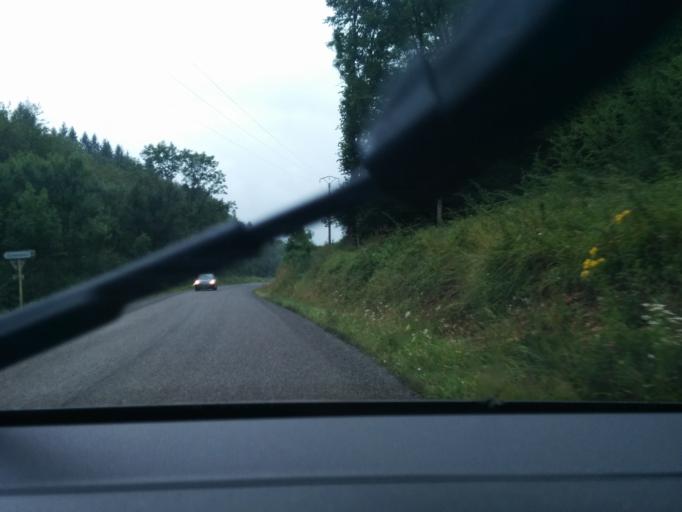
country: FR
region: Franche-Comte
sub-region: Departement du Jura
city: Valfin-les-Saint-Claude
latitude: 46.4446
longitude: 5.8221
